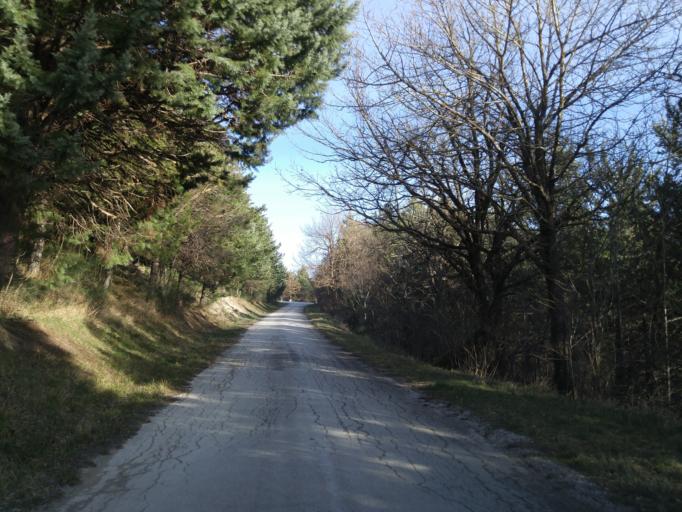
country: IT
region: The Marches
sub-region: Provincia di Pesaro e Urbino
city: Canavaccio
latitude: 43.6770
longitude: 12.6794
